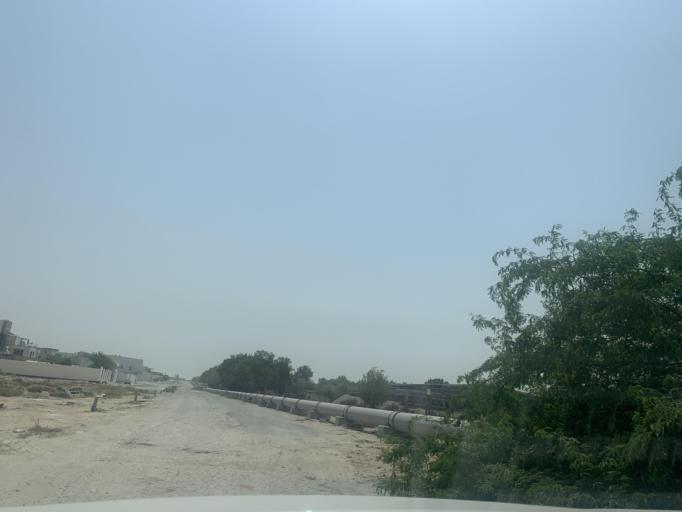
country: BH
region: Central Governorate
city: Madinat Hamad
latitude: 26.1440
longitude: 50.4712
